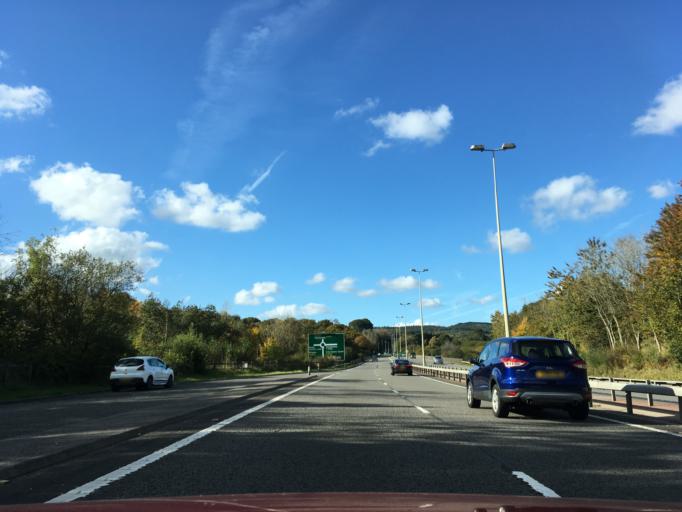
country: GB
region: Wales
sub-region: Merthyr Tydfil County Borough
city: Merthyr Tydfil
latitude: 51.7573
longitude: -3.4048
